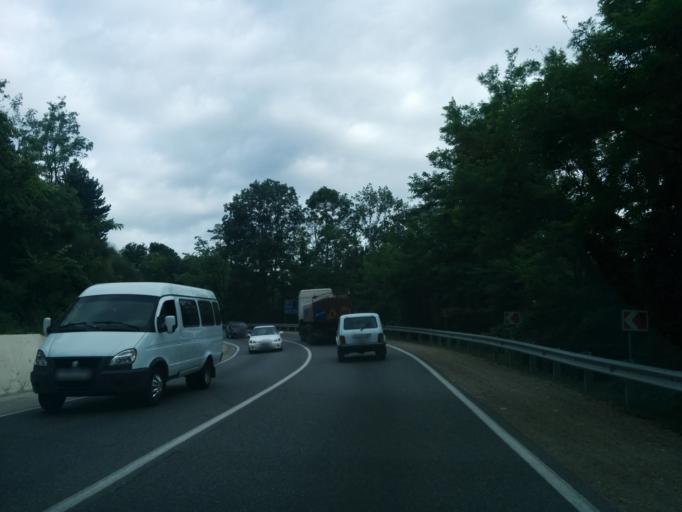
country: RU
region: Krasnodarskiy
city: Agoy
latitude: 44.1256
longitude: 39.0481
